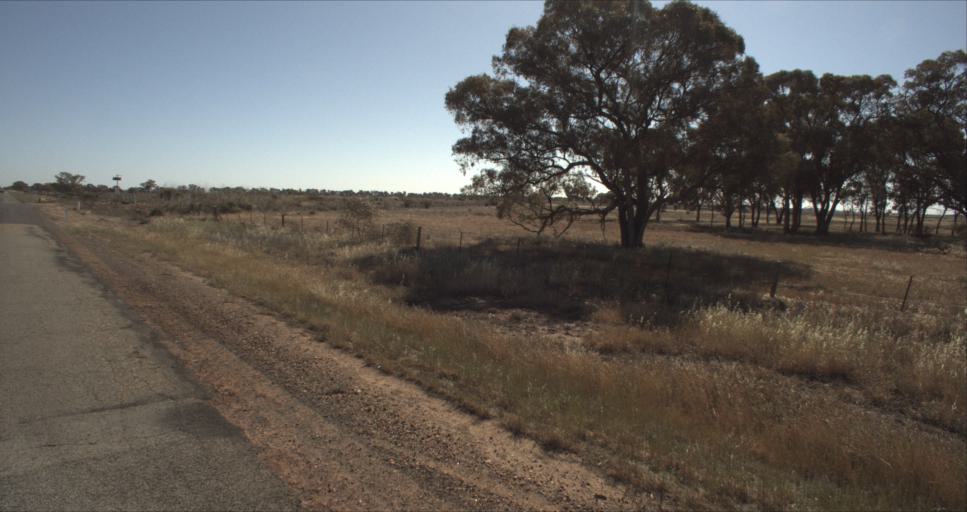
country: AU
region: New South Wales
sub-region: Leeton
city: Leeton
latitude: -34.5889
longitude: 146.2601
